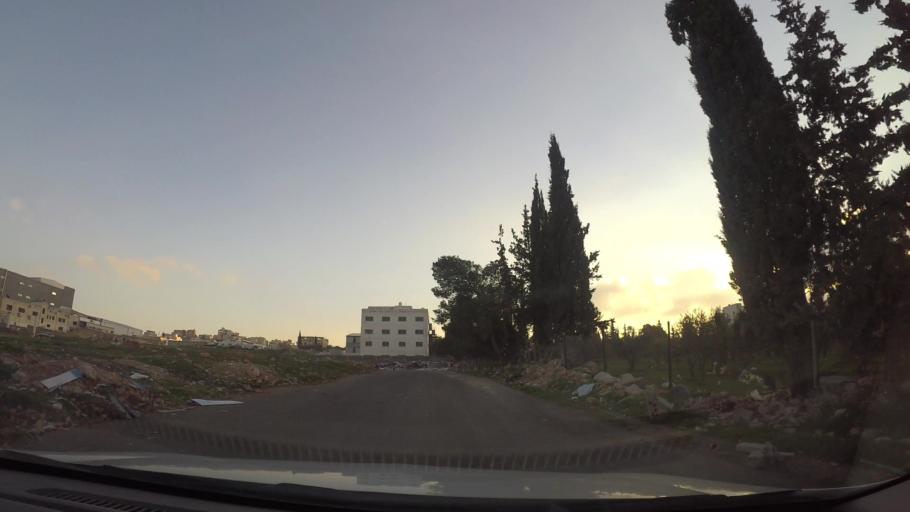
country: JO
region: Amman
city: Al Bunayyat ash Shamaliyah
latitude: 31.9118
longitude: 35.9171
